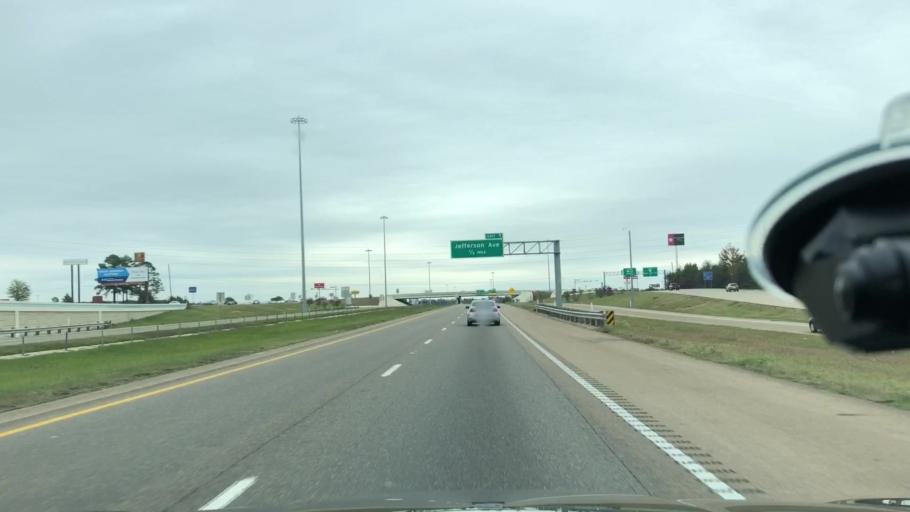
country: US
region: Arkansas
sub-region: Miller County
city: Texarkana
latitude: 33.4701
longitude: -94.0483
